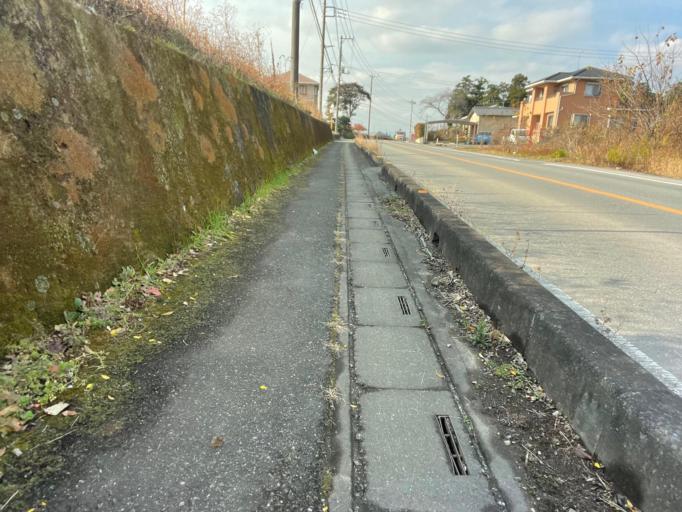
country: JP
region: Saitama
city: Yorii
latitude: 36.1567
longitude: 139.1898
